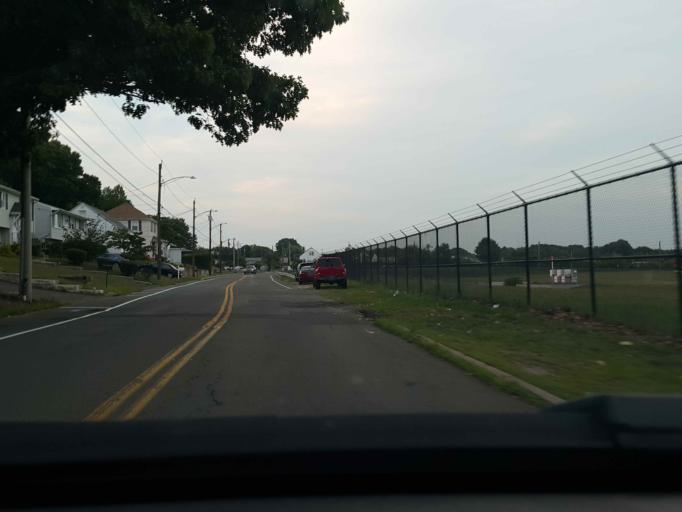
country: US
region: Connecticut
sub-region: New Haven County
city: East Haven
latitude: 41.2727
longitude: -72.8888
